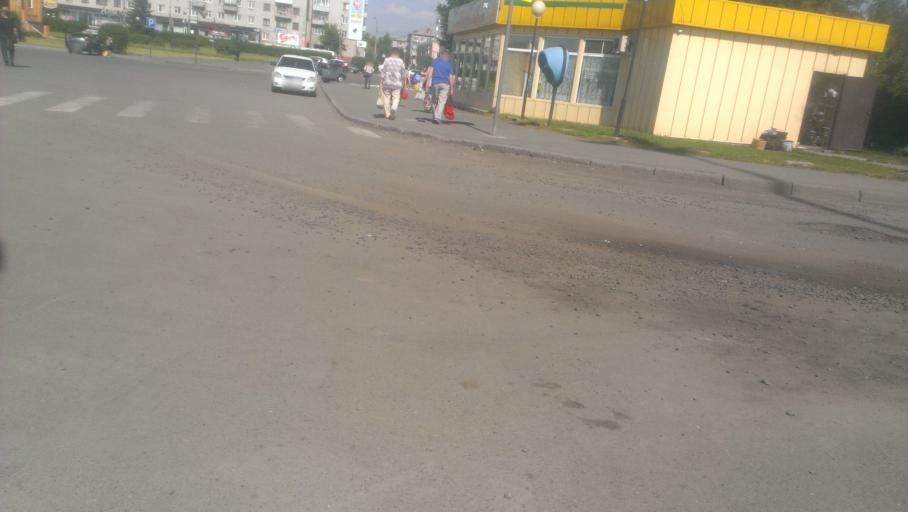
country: RU
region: Altai Krai
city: Novoaltaysk
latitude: 53.3916
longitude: 83.9322
